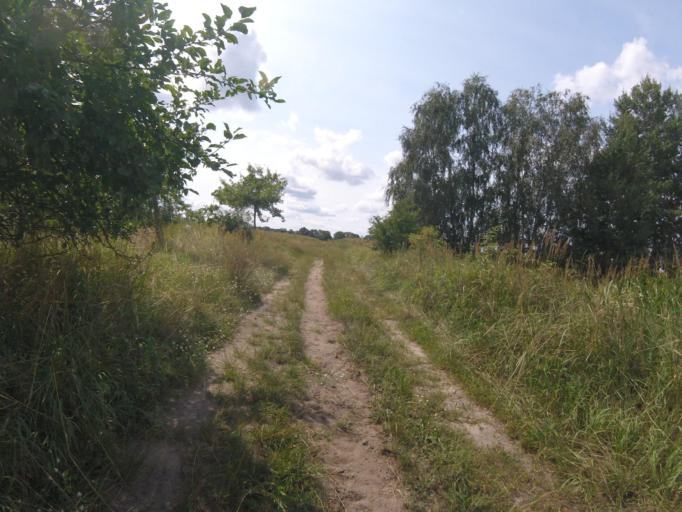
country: DE
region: Brandenburg
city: Mittenwalde
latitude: 52.2866
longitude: 13.5056
